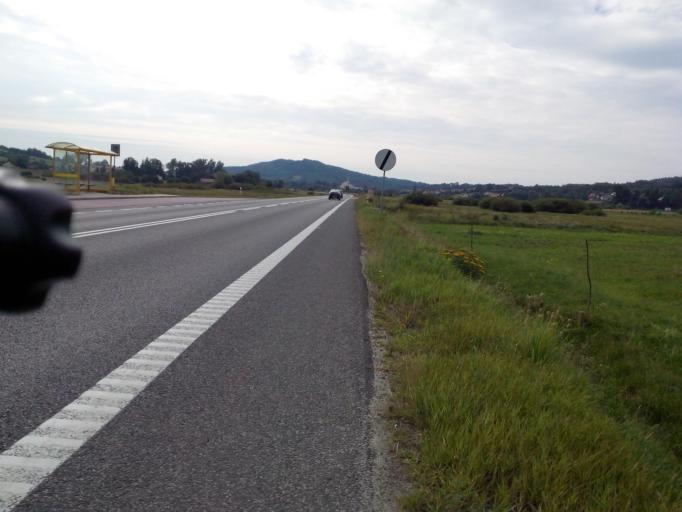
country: PL
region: Subcarpathian Voivodeship
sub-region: Powiat brzozowski
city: Domaradz
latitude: 49.8024
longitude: 21.9274
